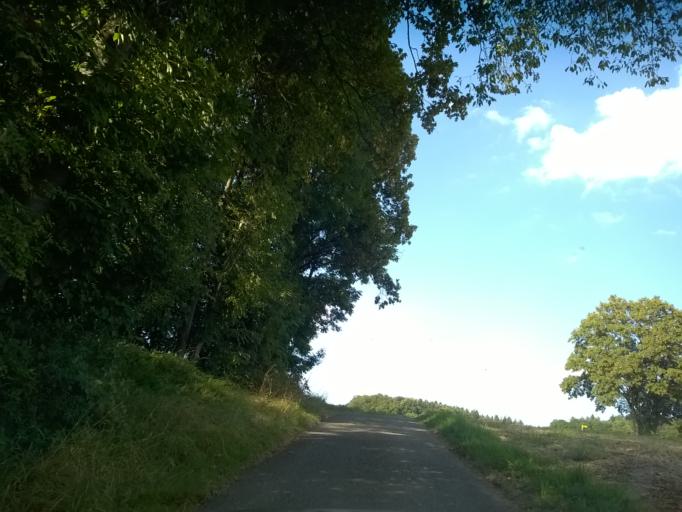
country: CH
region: Zurich
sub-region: Bezirk Buelach
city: Embrach / Embrach (Dorfkern)
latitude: 47.4928
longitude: 8.6176
